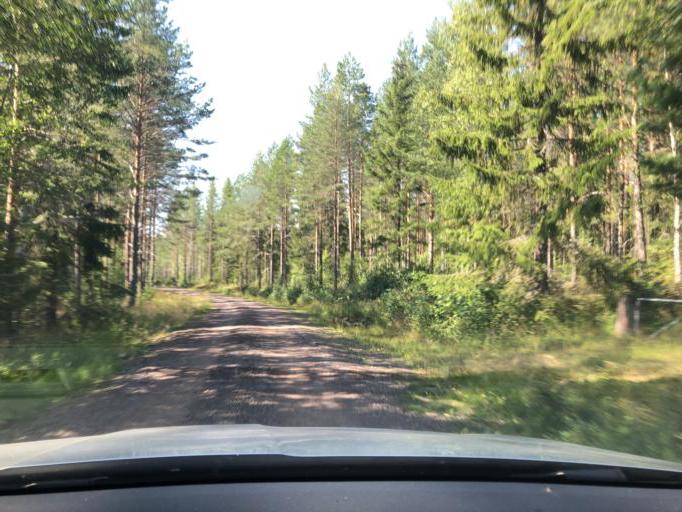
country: SE
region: Dalarna
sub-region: Orsa Kommun
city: Orsa
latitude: 61.2203
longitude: 14.7186
